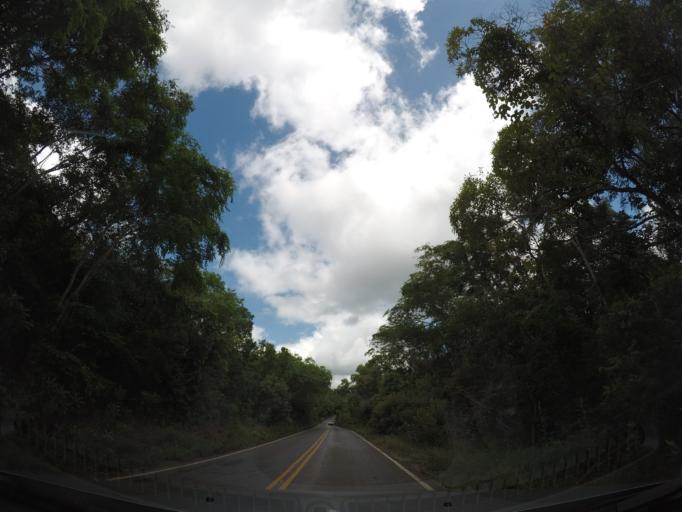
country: BR
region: Bahia
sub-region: Andarai
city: Vera Cruz
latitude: -12.5080
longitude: -41.3615
